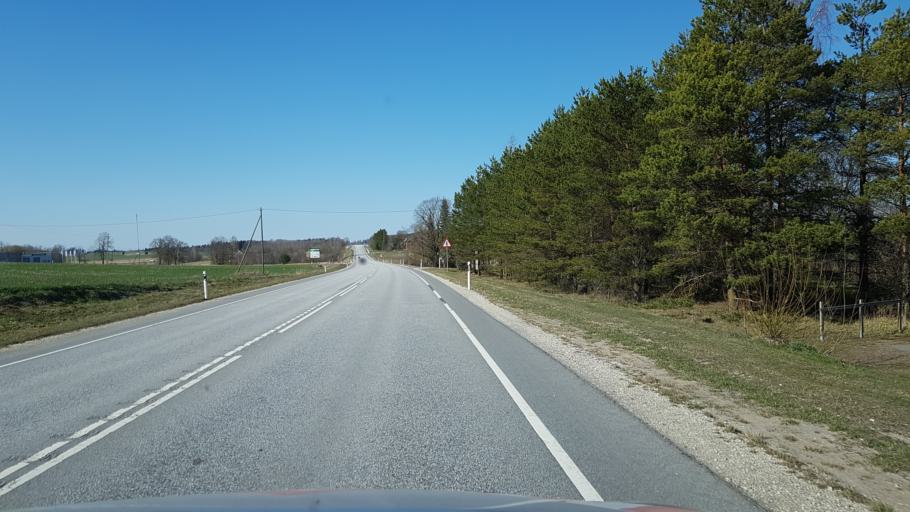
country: EE
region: Tartu
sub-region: Tartu linn
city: Tartu
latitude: 58.4904
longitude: 26.7771
